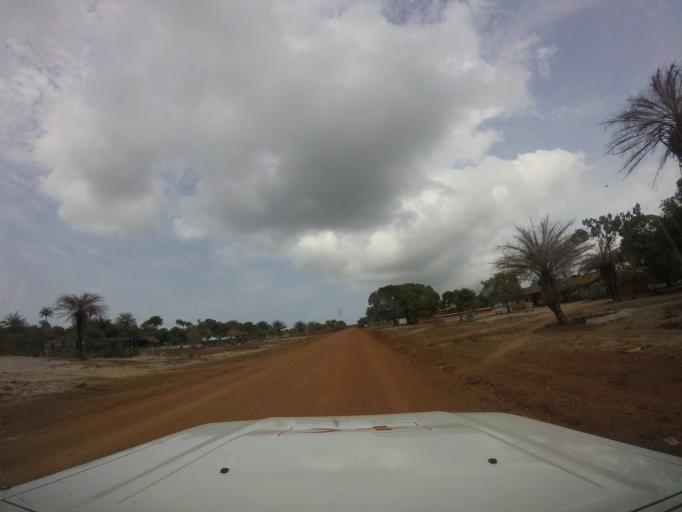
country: LR
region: Grand Cape Mount
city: Robertsport
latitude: 6.6914
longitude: -11.2677
